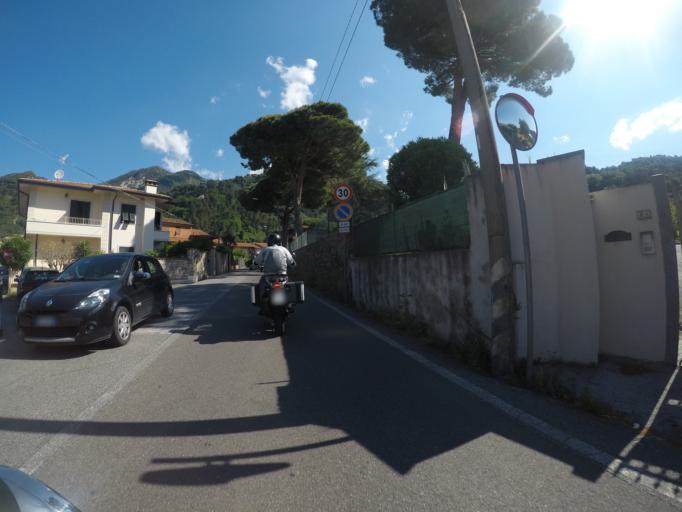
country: IT
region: Tuscany
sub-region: Provincia di Massa-Carrara
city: Massa
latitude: 44.0426
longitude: 10.1428
